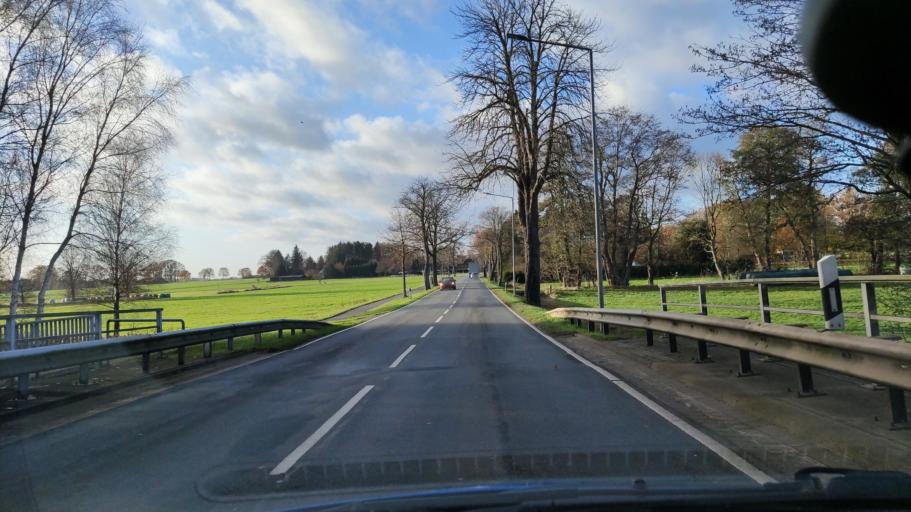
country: DE
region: Lower Saxony
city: Soltau
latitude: 53.0278
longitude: 9.8437
